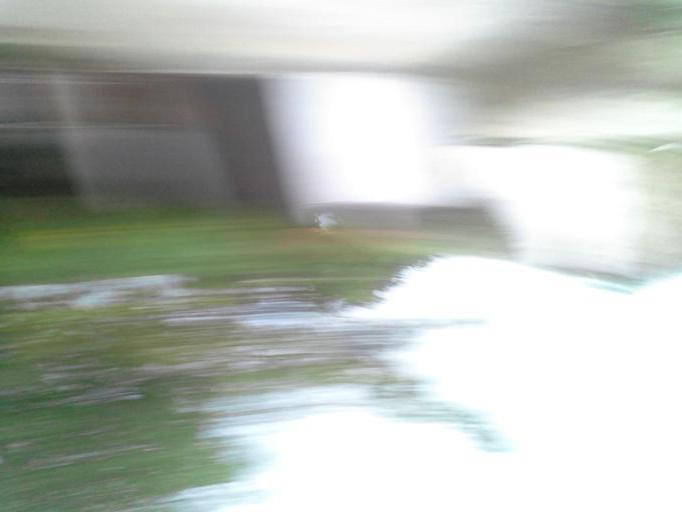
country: CO
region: Sucre
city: Los Palmitos
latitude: 9.3766
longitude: -75.2721
